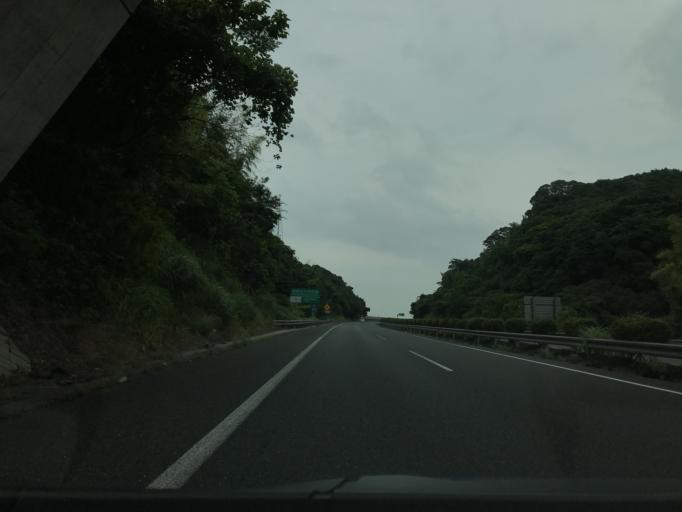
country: JP
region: Fukuoka
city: Kanda
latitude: 33.7994
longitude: 130.9561
